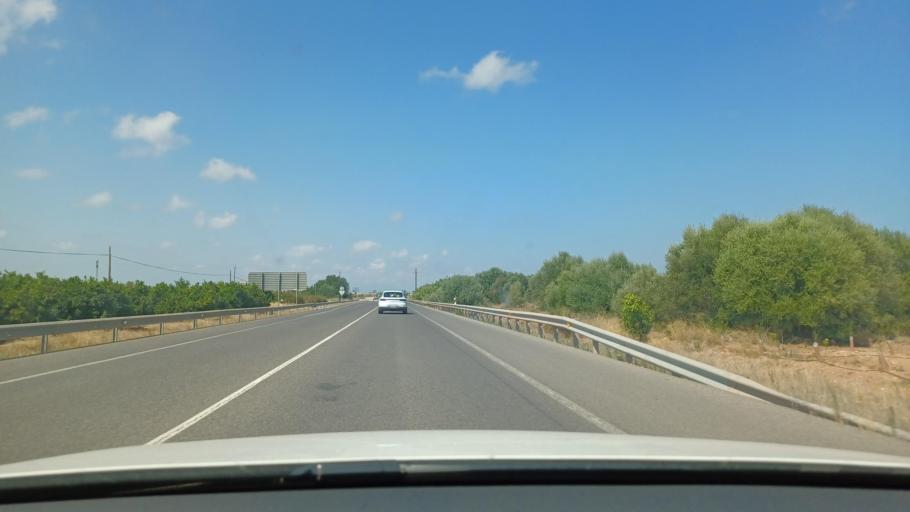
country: ES
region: Valencia
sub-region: Provincia de Castello
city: Moncofar
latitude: 39.8091
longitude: -0.1704
